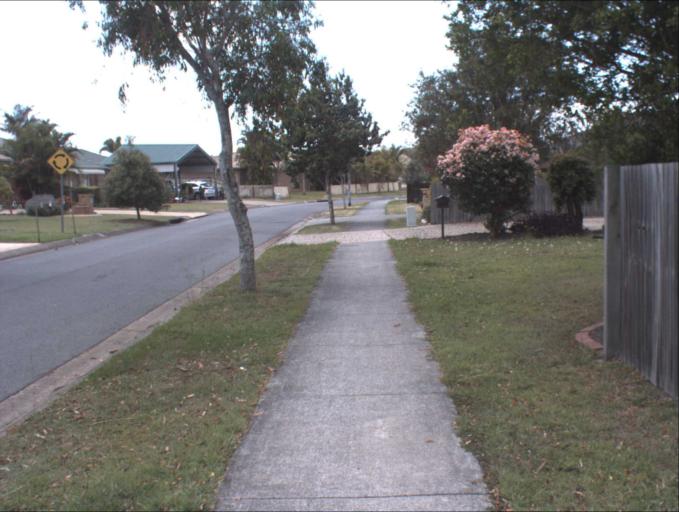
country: AU
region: Queensland
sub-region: Logan
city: Slacks Creek
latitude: -27.6697
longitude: 153.1506
